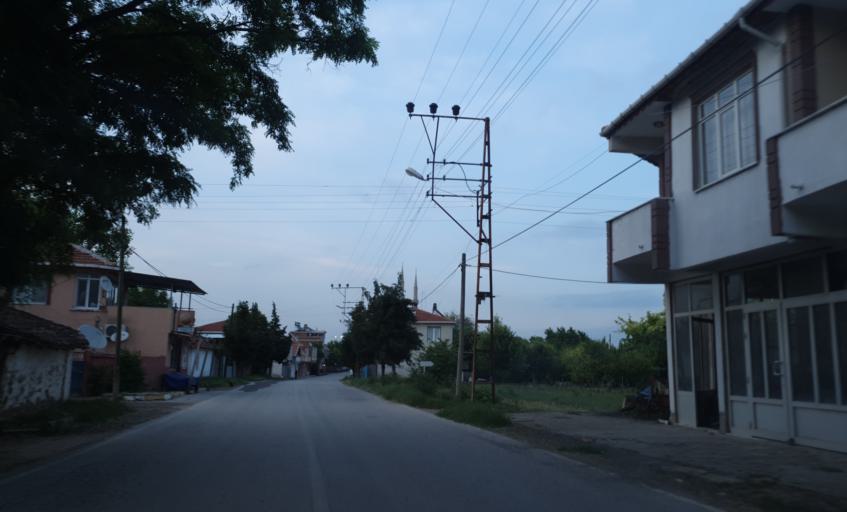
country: TR
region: Tekirdag
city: Beyazkoy
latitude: 41.3820
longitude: 27.6172
